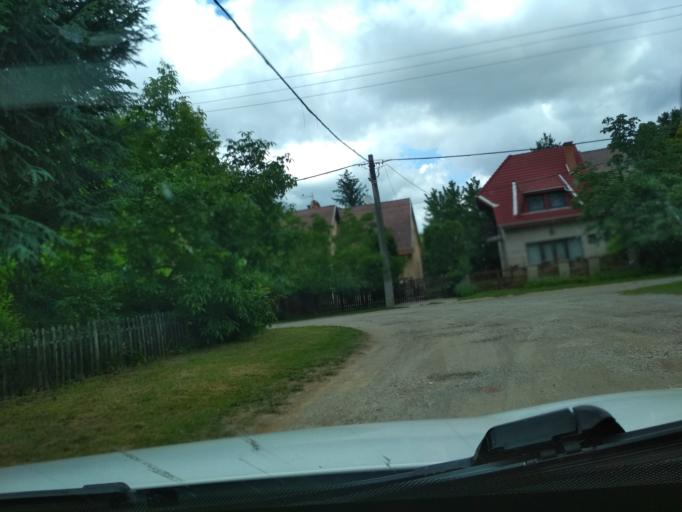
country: HU
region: Jasz-Nagykun-Szolnok
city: Tiszafured
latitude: 47.6190
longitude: 20.7385
